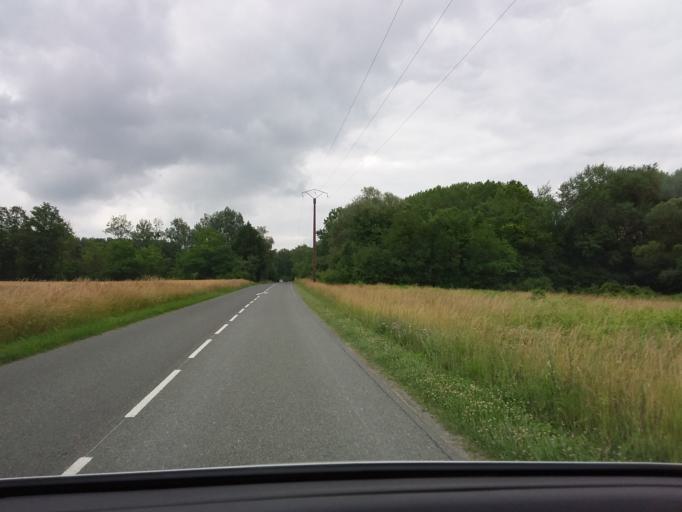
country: FR
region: Picardie
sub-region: Departement de l'Aisne
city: Vailly-sur-Aisne
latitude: 49.4004
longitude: 3.6188
